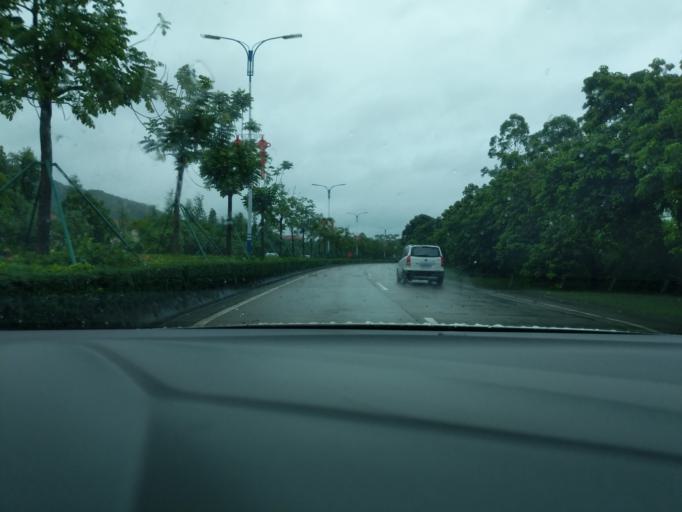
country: CN
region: Guangdong
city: Pingshi
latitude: 22.2154
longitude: 112.3184
